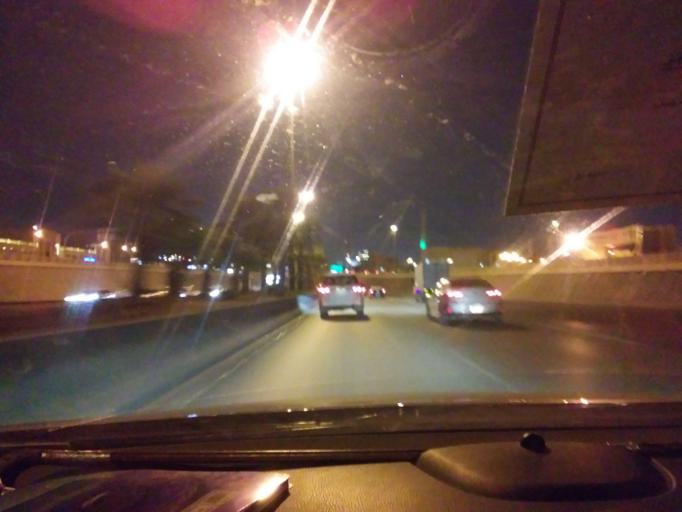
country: SA
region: Ar Riyad
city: Riyadh
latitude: 24.6642
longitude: 46.7866
